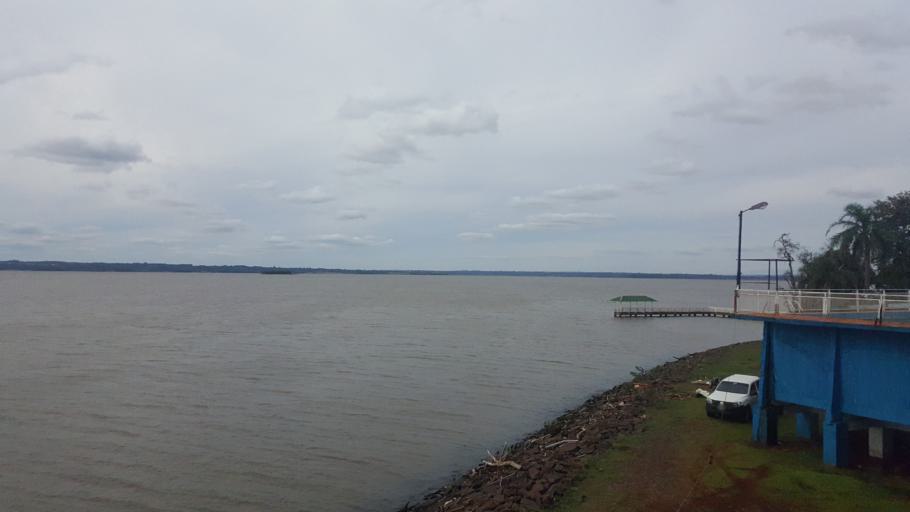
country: PY
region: Itapua
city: San Juan del Parana
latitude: -27.3601
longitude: -55.9573
